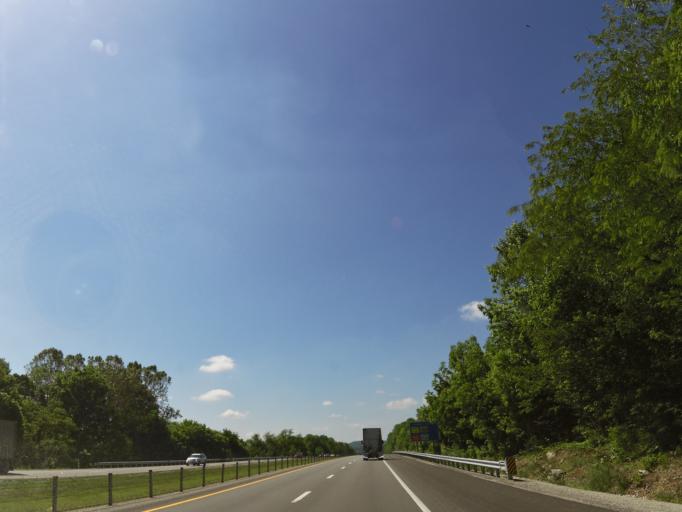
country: US
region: Kentucky
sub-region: Rockcastle County
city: Mount Vernon
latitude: 37.4036
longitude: -84.3390
